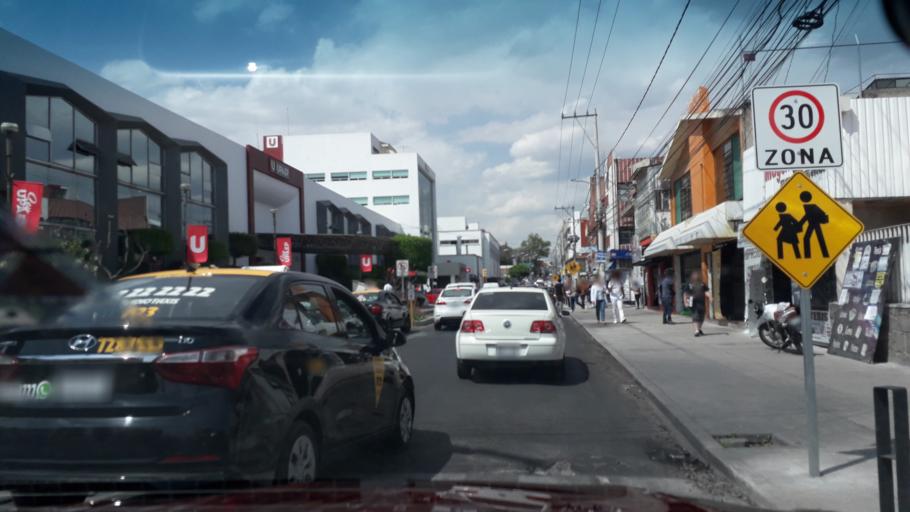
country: MX
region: Puebla
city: Puebla
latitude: 19.0475
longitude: -98.2162
